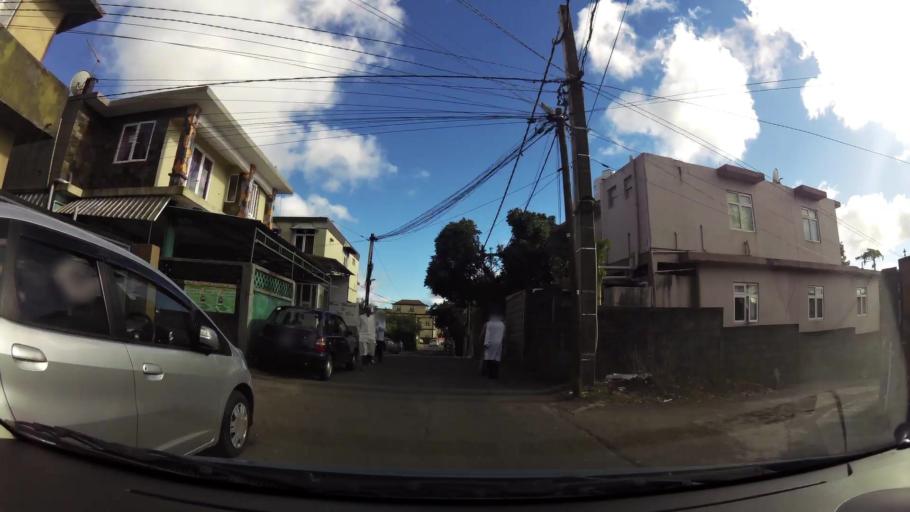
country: MU
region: Plaines Wilhems
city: Curepipe
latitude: -20.3066
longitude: 57.5224
